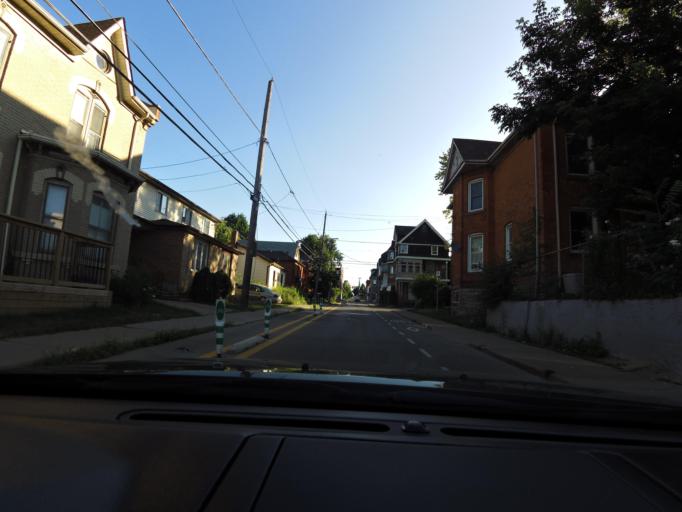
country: CA
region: Ontario
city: Hamilton
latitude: 43.2597
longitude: -79.8837
